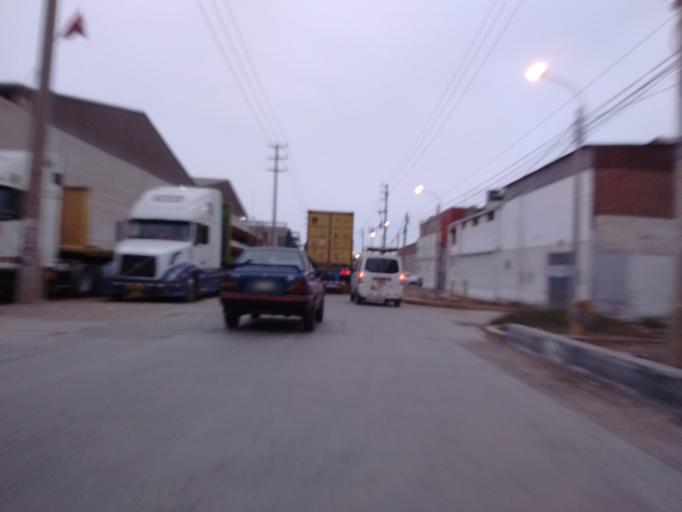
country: PE
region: Callao
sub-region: Callao
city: Callao
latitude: -12.0445
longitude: -77.0778
